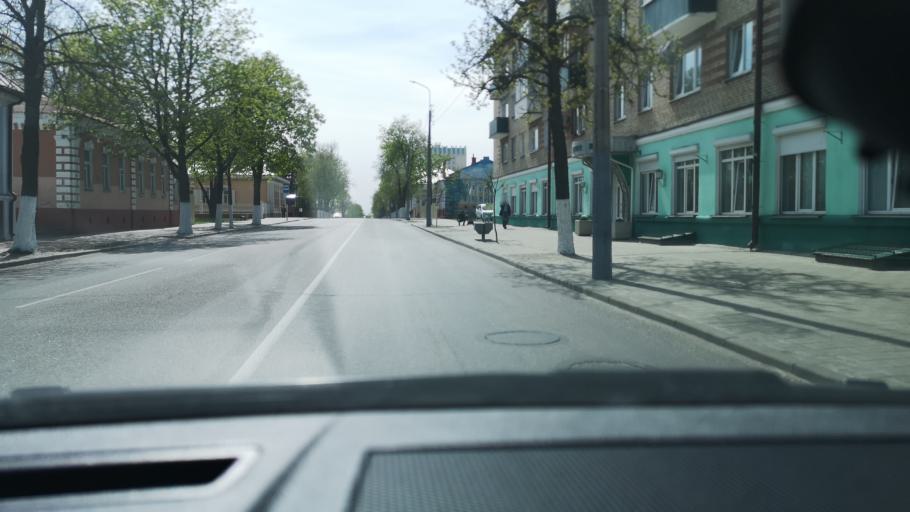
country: BY
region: Gomel
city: Gomel
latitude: 52.4190
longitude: 31.0094
